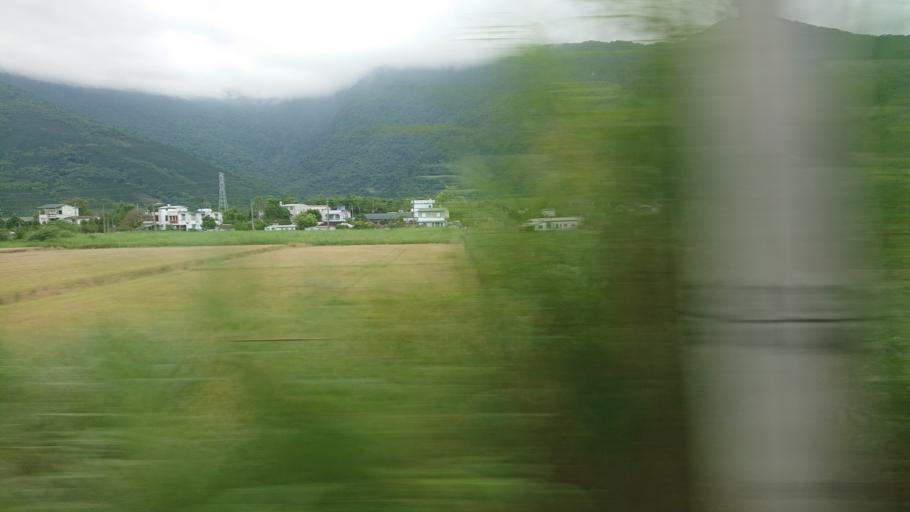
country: TW
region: Taiwan
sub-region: Hualien
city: Hualian
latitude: 23.7506
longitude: 121.4490
